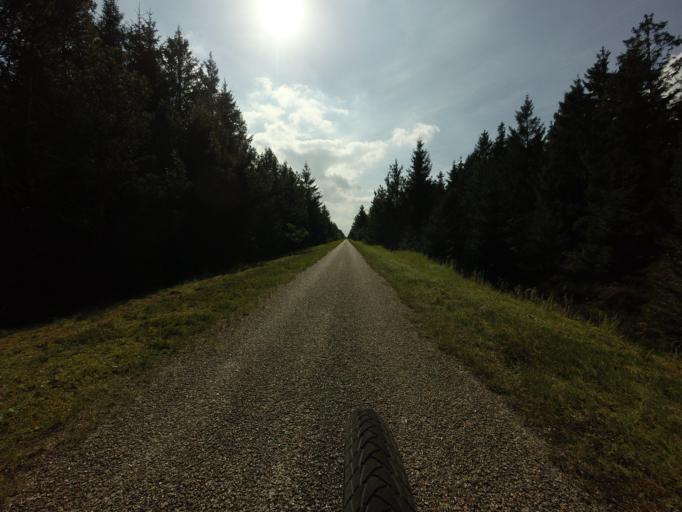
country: DK
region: Central Jutland
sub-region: Viborg Kommune
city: Karup
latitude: 56.2599
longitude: 9.1090
